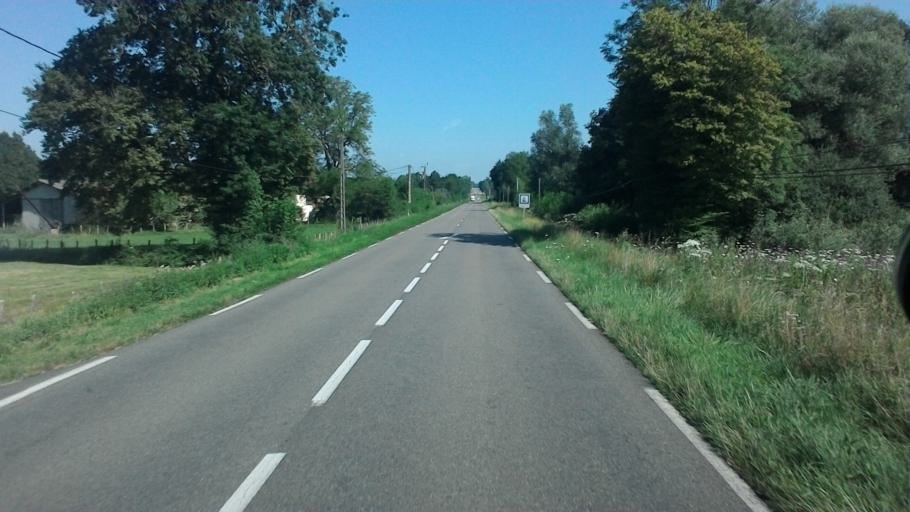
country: FR
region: Rhone-Alpes
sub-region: Departement de l'Ain
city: Saint-Trivier-de-Courtes
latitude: 46.4150
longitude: 5.1033
